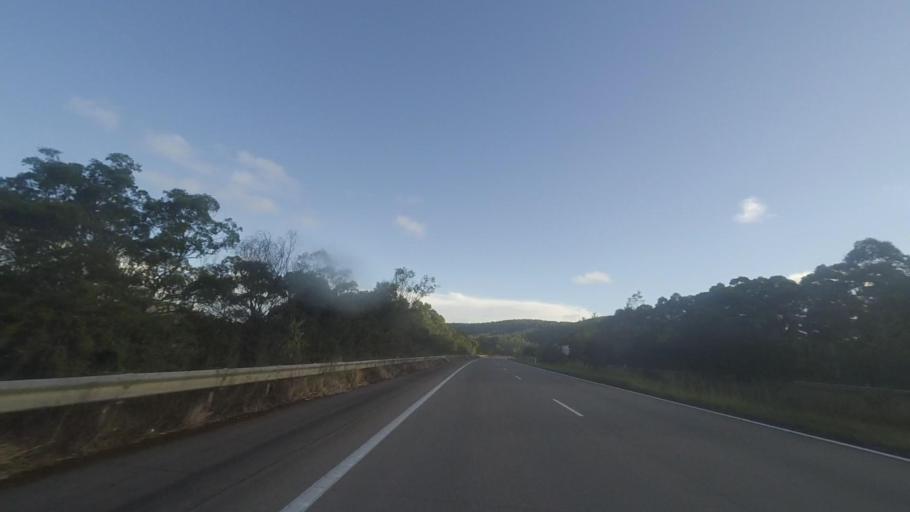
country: AU
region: New South Wales
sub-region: Great Lakes
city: Nabiac
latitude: -32.2641
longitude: 152.3280
